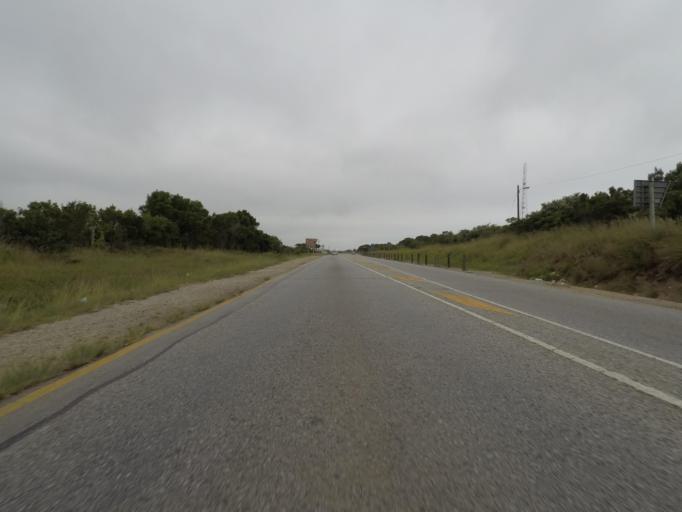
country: ZA
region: Eastern Cape
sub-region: Cacadu District Municipality
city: Port Alfred
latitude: -33.6798
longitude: 26.6645
